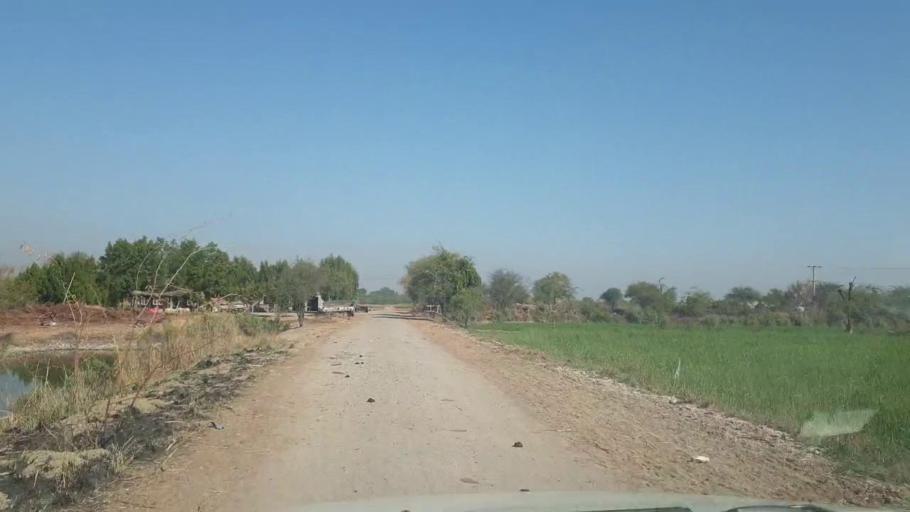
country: PK
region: Sindh
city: Mirpur Khas
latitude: 25.5095
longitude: 69.1371
